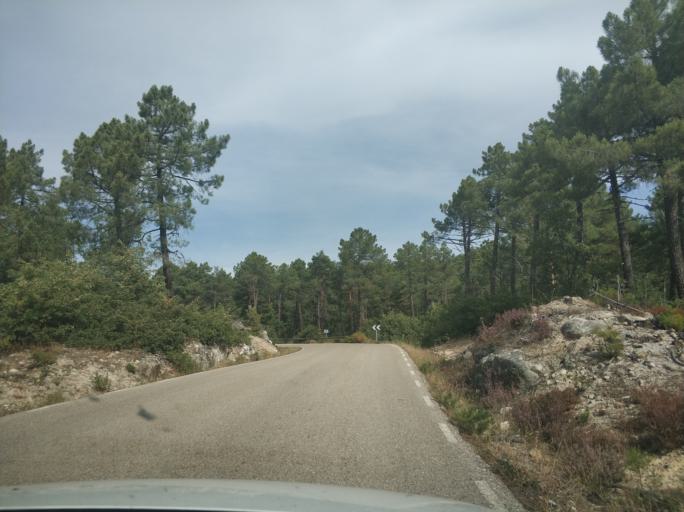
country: ES
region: Castille and Leon
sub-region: Provincia de Soria
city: Duruelo de la Sierra
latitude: 41.8901
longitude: -2.9415
